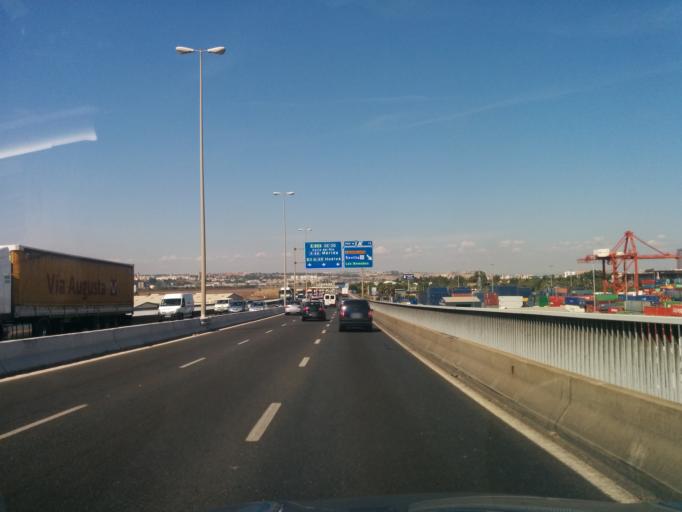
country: ES
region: Andalusia
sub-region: Provincia de Sevilla
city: Gelves
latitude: 37.3537
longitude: -5.9985
